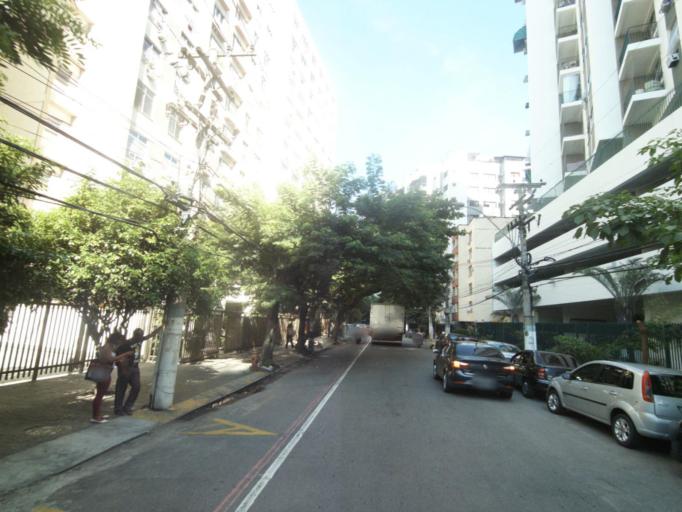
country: BR
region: Rio de Janeiro
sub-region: Niteroi
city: Niteroi
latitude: -22.9014
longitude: -43.1242
